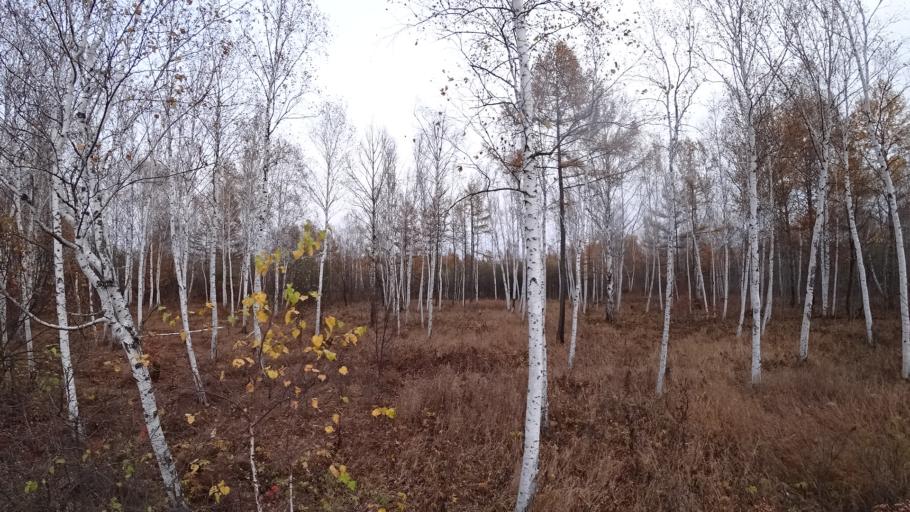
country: RU
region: Khabarovsk Krai
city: Amursk
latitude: 49.9843
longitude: 136.3155
